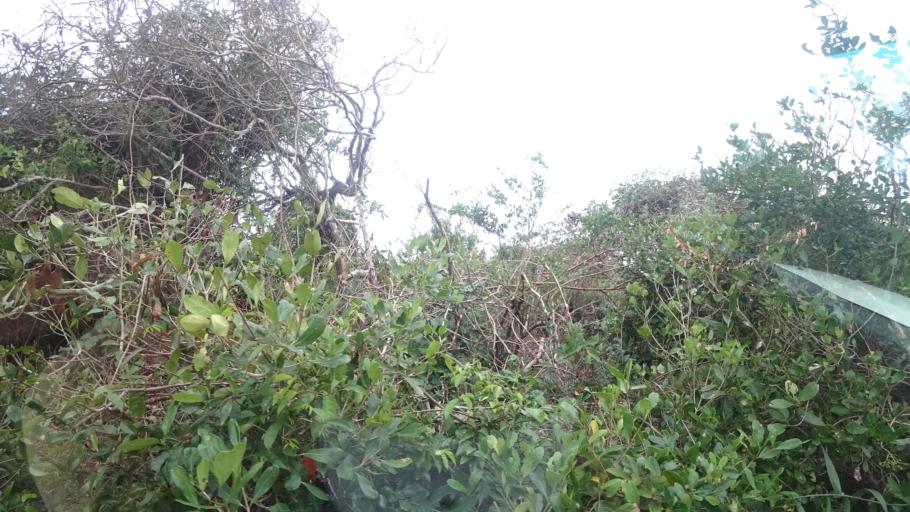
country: MZ
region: Sofala
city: Beira
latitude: -19.6164
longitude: 35.2167
